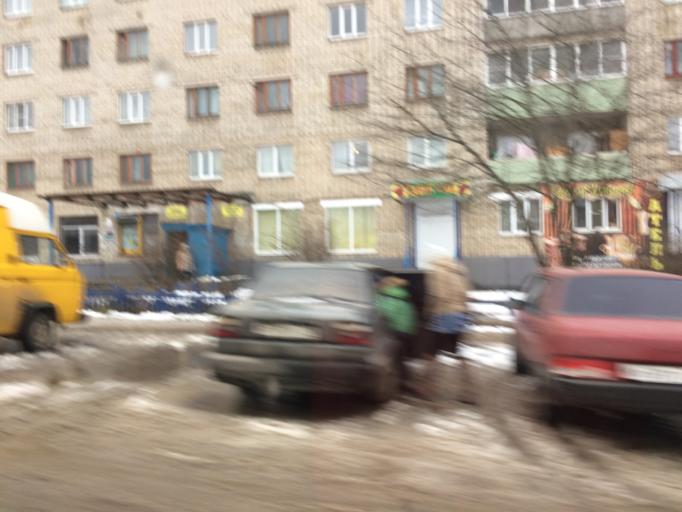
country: RU
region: Tula
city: Suvorov
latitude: 54.1193
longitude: 36.5045
